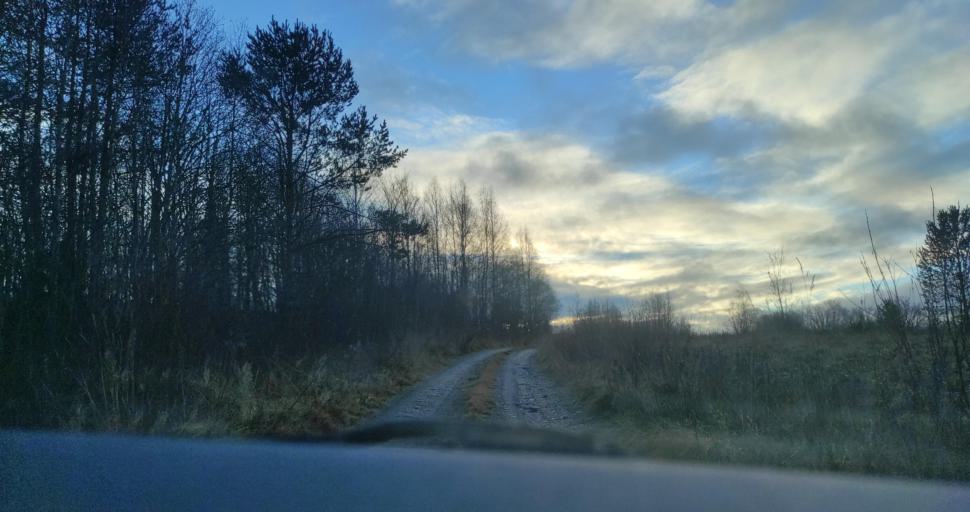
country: RU
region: Republic of Karelia
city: Pitkyaranta
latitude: 61.7287
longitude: 31.3817
